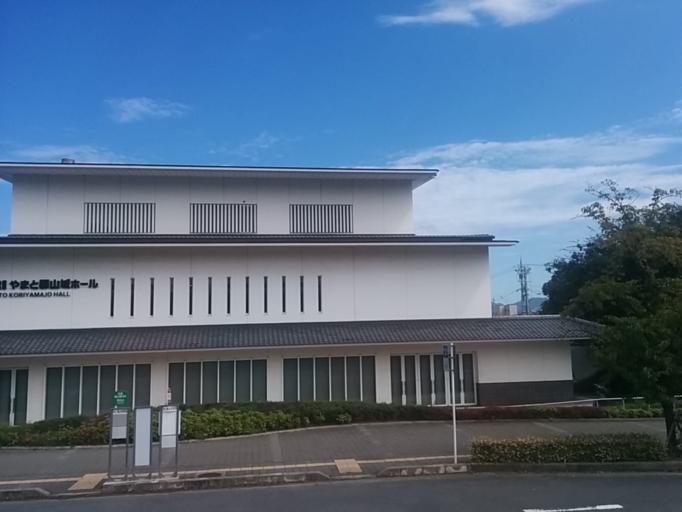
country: JP
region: Nara
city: Nara-shi
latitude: 34.6517
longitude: 135.7817
